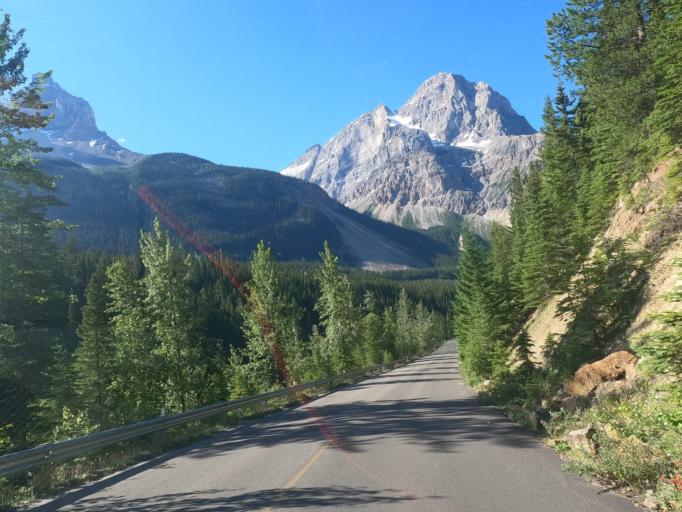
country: CA
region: Alberta
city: Lake Louise
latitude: 51.4323
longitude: -116.4225
